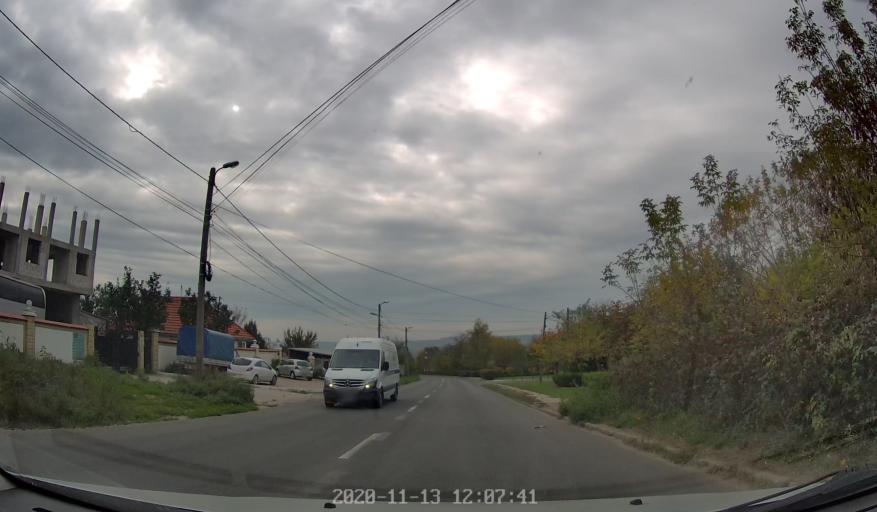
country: MD
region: Chisinau
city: Chisinau
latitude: 46.9723
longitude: 28.8342
